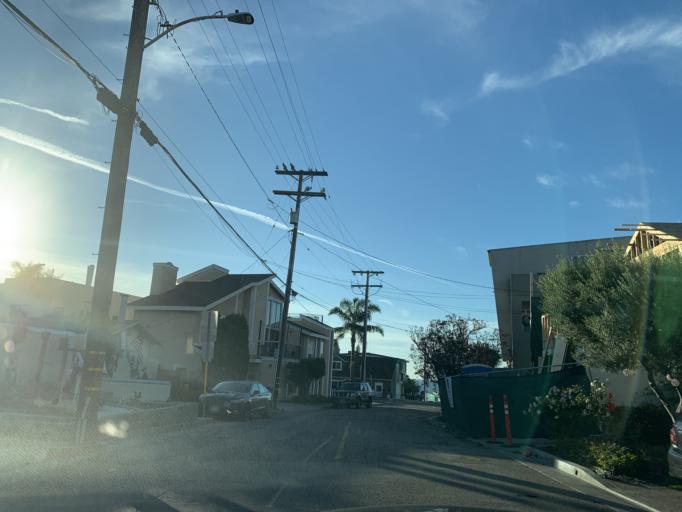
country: US
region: California
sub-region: Los Angeles County
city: Hermosa Beach
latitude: 33.8707
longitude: -118.4008
